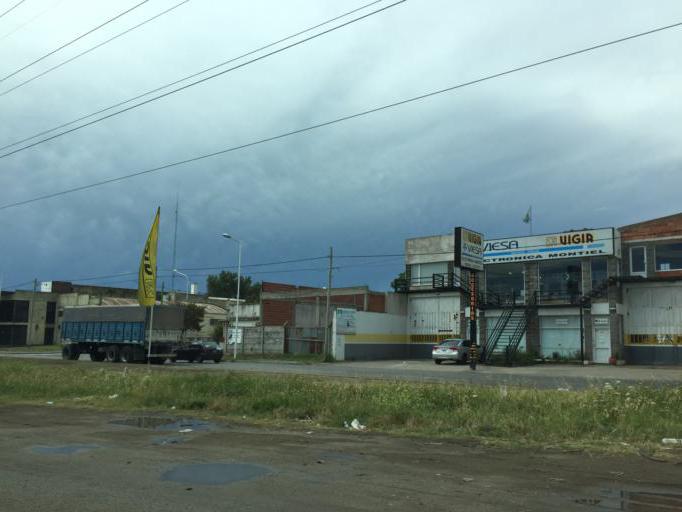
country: AR
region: Buenos Aires
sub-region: Partido de Tandil
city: Tandil
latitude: -37.3111
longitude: -59.1144
